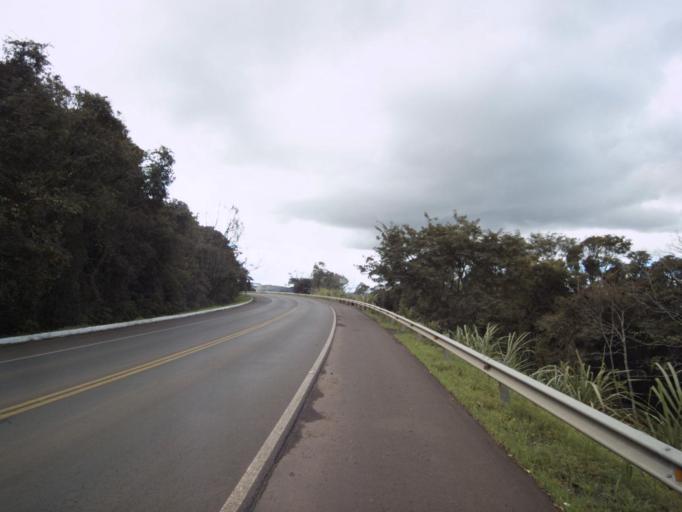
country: BR
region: Santa Catarina
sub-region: Concordia
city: Concordia
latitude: -27.2621
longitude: -51.9549
